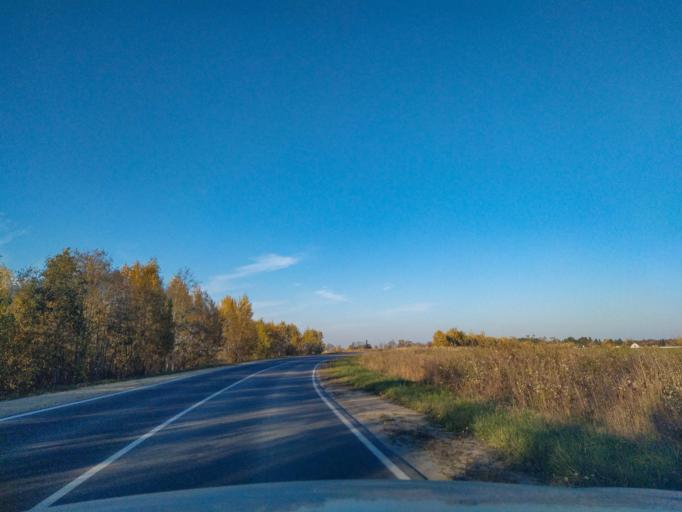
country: RU
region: Leningrad
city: Siverskiy
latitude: 59.3164
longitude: 30.0340
